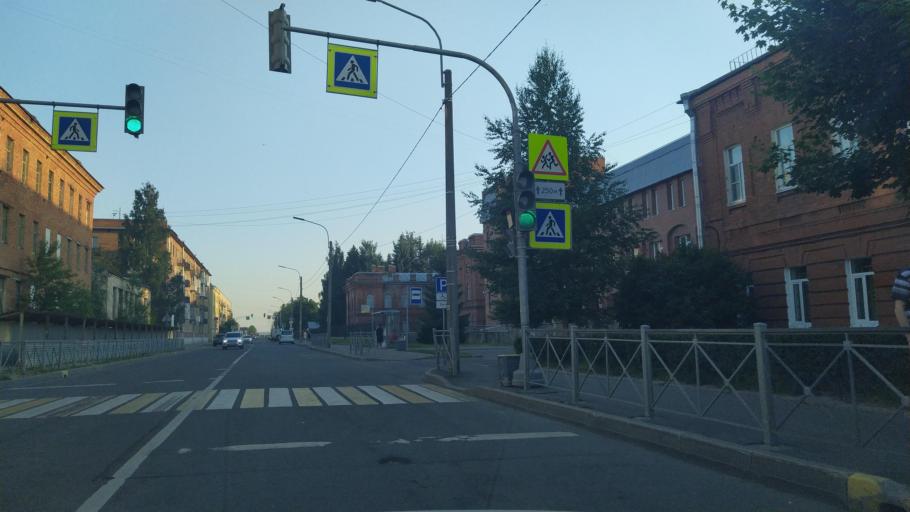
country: RU
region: St.-Petersburg
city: Kronshtadt
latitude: 59.9965
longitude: 29.7585
